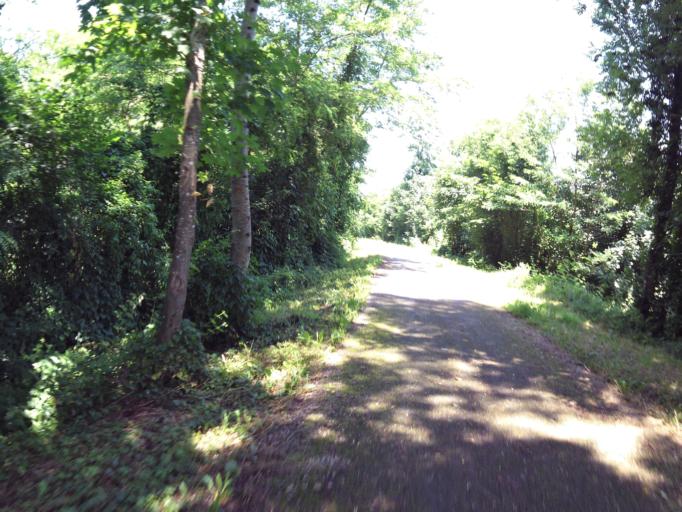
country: FR
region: Aquitaine
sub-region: Departement des Pyrenees-Atlantiques
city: Salies-de-Bearn
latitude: 43.4452
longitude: -0.9935
